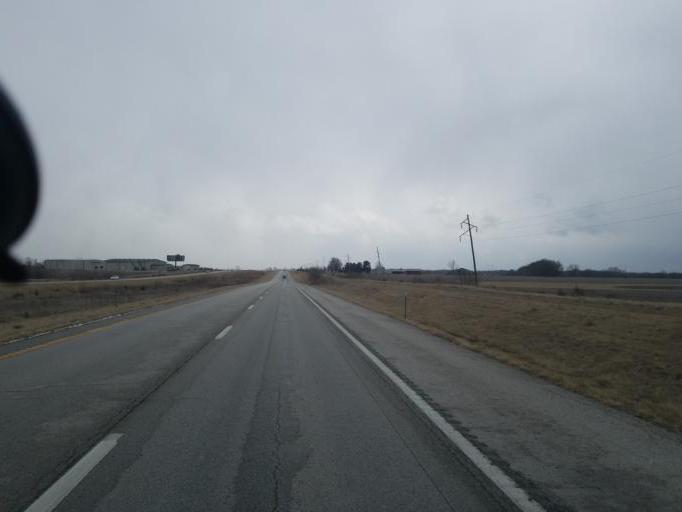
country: US
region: Missouri
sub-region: Randolph County
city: Moberly
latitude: 39.5462
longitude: -92.4525
